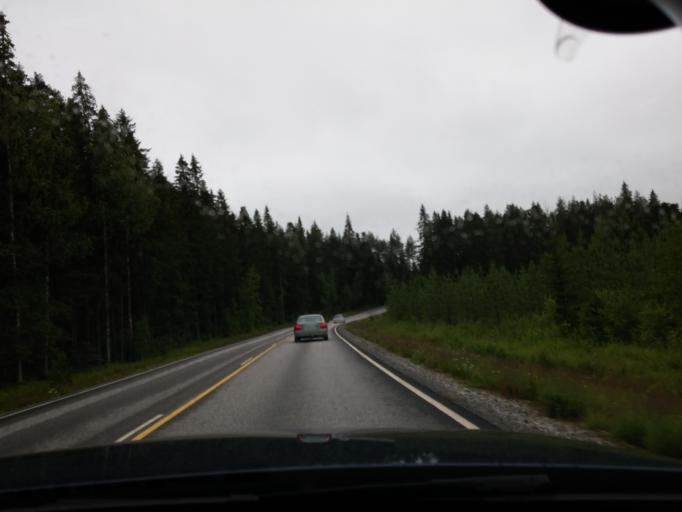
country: FI
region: Central Finland
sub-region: Saarijaervi-Viitasaari
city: Pylkoenmaeki
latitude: 62.5680
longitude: 24.6174
